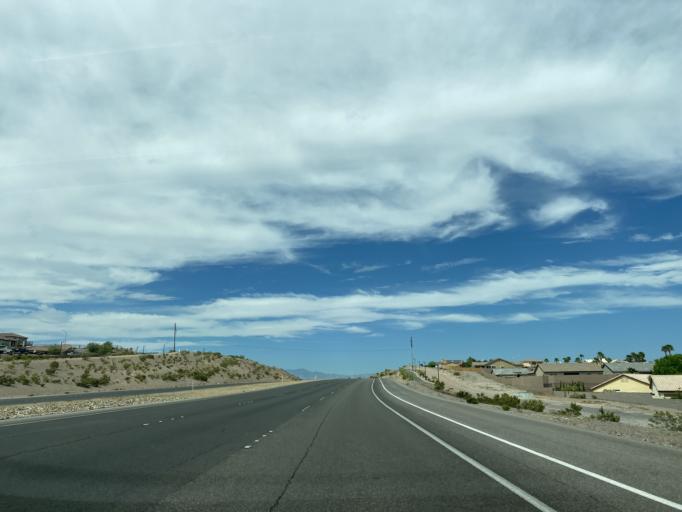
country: US
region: Nevada
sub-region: Clark County
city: Henderson
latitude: 36.0773
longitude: -114.9413
